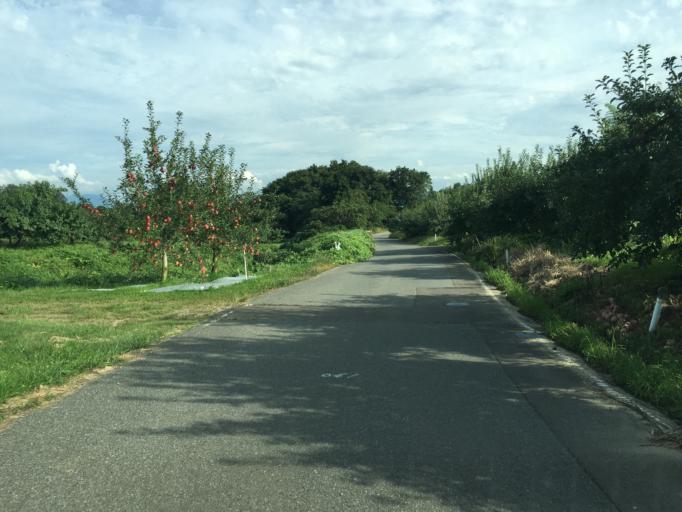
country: JP
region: Fukushima
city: Hobaramachi
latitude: 37.8351
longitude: 140.4697
